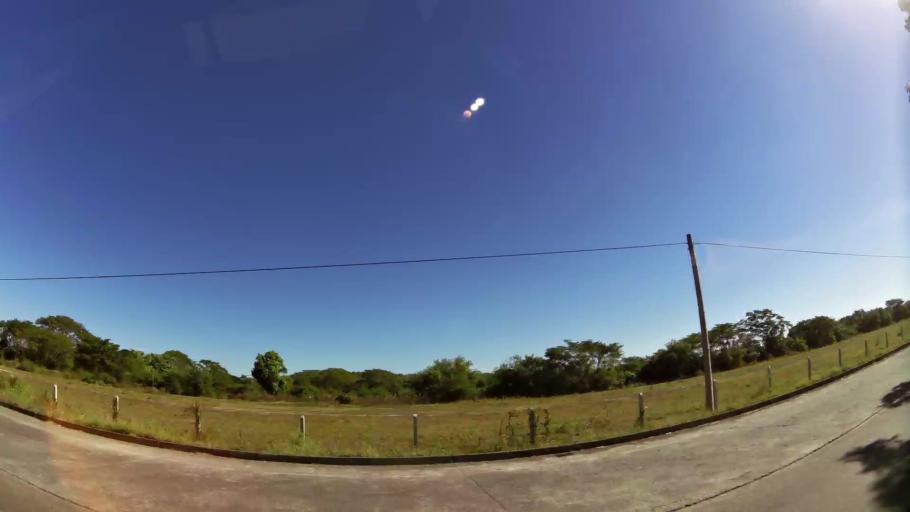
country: SV
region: San Miguel
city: San Miguel
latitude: 13.4450
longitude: -88.1294
